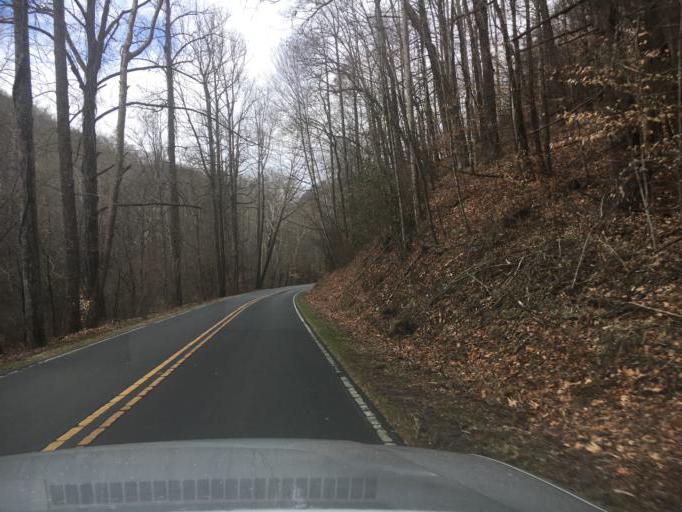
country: US
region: North Carolina
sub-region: Transylvania County
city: Brevard
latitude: 35.2898
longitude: -82.7646
